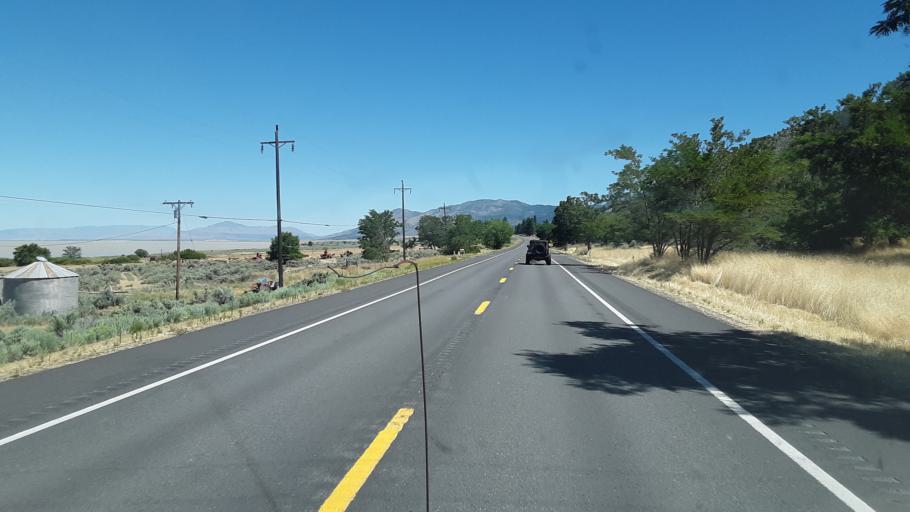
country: US
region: California
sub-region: Lassen County
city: Janesville
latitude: 40.2307
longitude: -120.4426
